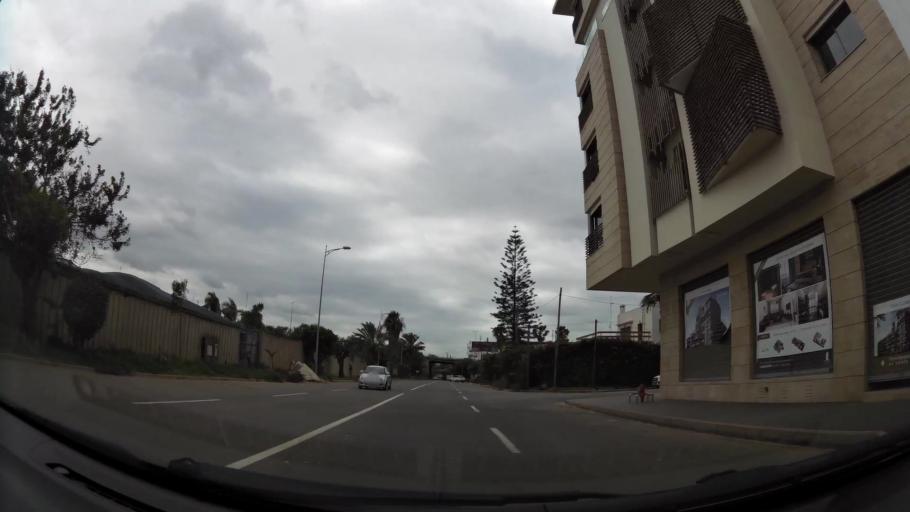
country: MA
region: Grand Casablanca
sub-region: Casablanca
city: Casablanca
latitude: 33.5527
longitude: -7.6331
